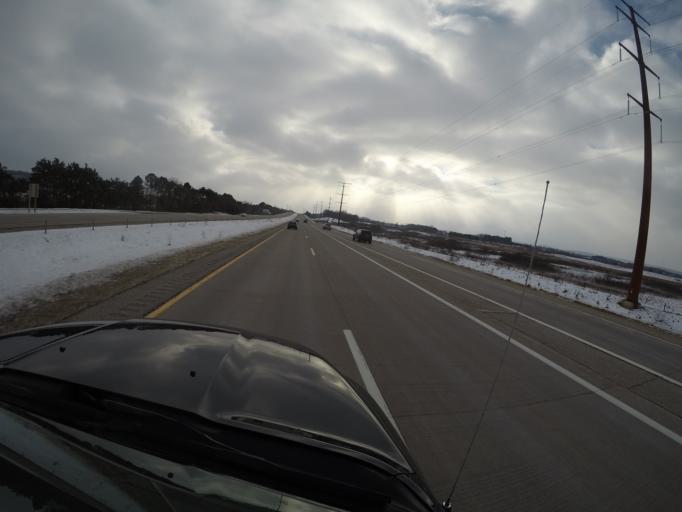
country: US
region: Wisconsin
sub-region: La Crosse County
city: Holmen
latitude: 43.9928
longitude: -91.2863
